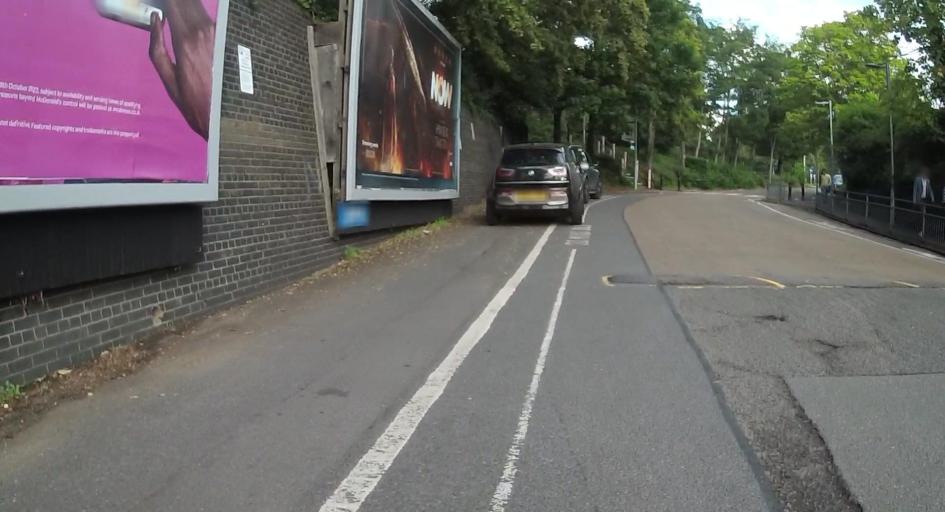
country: GB
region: England
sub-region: Surrey
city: Weybridge
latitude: 51.3620
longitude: -0.4578
